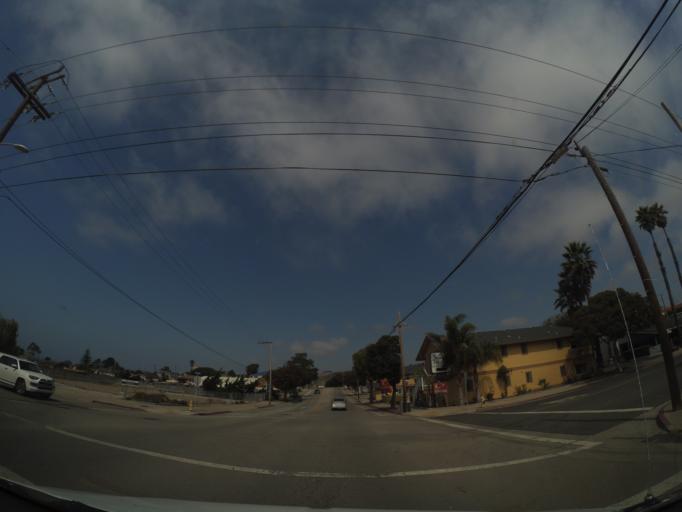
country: US
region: California
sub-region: San Luis Obispo County
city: Morro Bay
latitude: 35.3686
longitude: -120.8500
